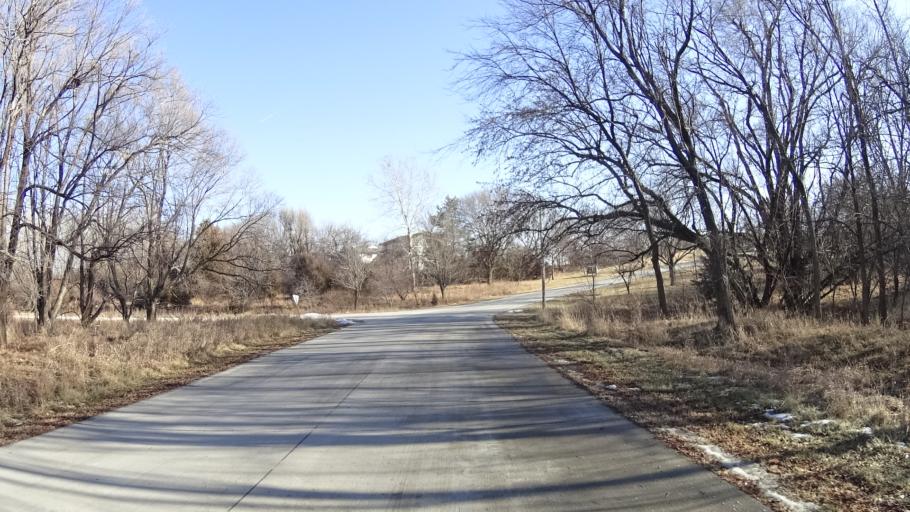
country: US
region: Nebraska
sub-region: Douglas County
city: Bennington
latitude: 41.3081
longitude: -96.1310
